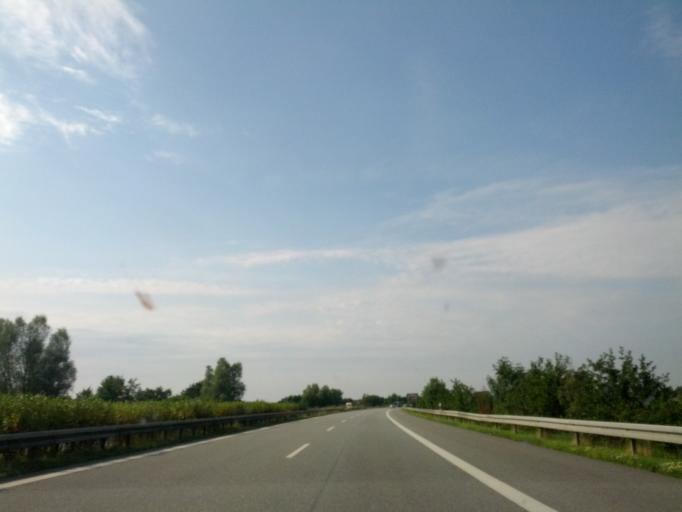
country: DE
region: Mecklenburg-Vorpommern
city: Muhl Rosin
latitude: 53.8545
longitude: 12.2661
